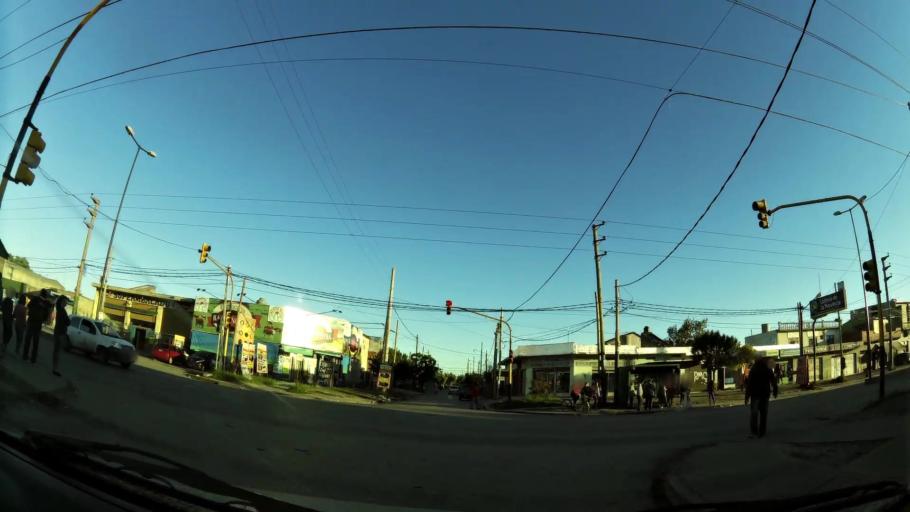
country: AR
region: Buenos Aires
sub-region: Partido de Almirante Brown
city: Adrogue
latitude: -34.7801
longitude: -58.3365
